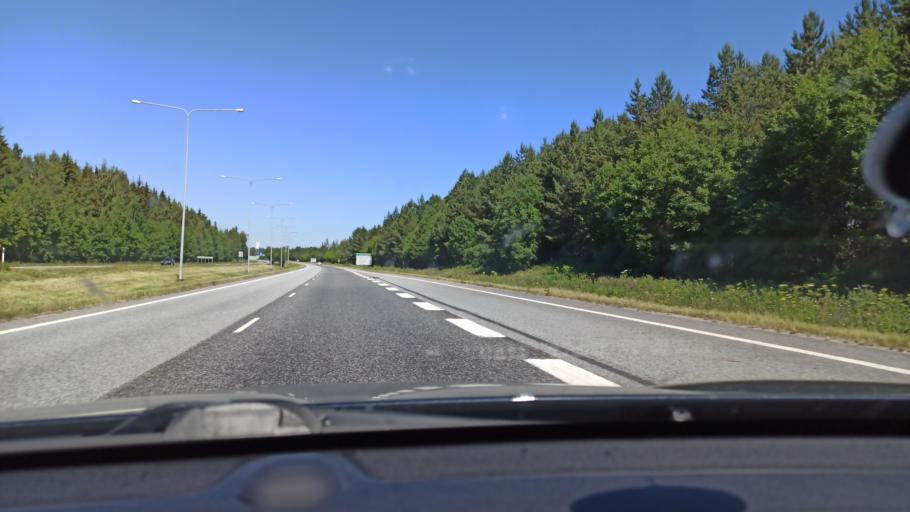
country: FI
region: Ostrobothnia
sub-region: Vaasa
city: Ristinummi
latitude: 63.0587
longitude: 21.7111
